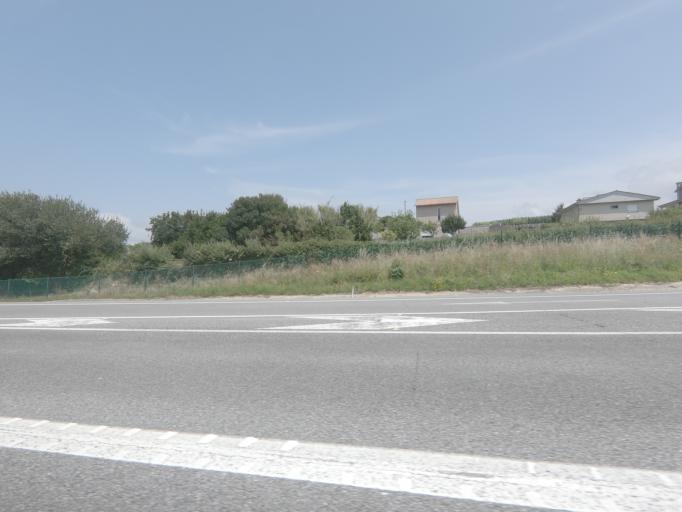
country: ES
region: Galicia
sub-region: Provincia de Pontevedra
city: Baiona
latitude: 42.1015
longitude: -8.8247
